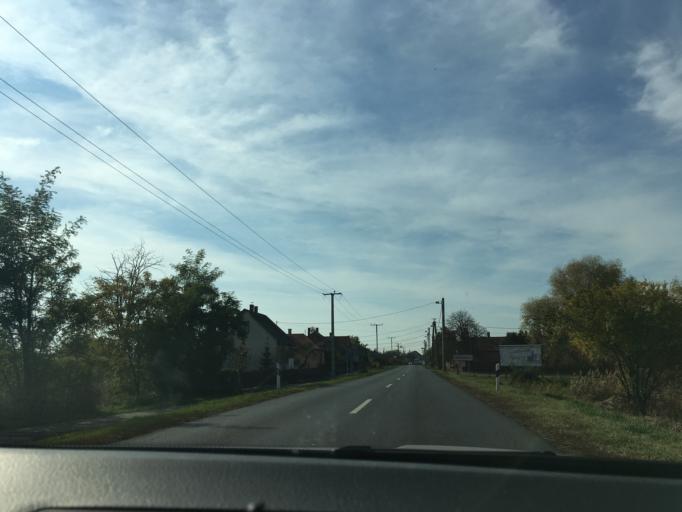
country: HU
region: Hajdu-Bihar
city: Vamospercs
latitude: 47.5247
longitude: 21.9113
